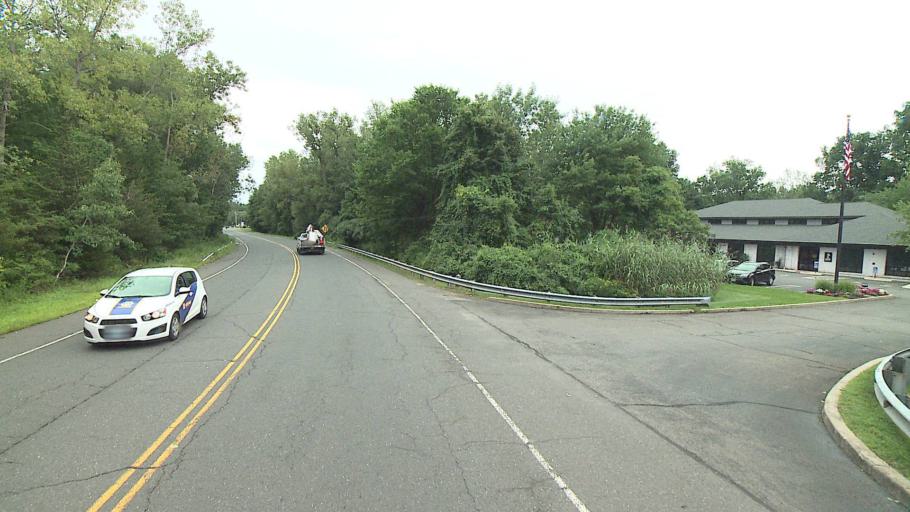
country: US
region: Connecticut
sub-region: Middlesex County
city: Cromwell
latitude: 41.6016
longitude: -72.6804
